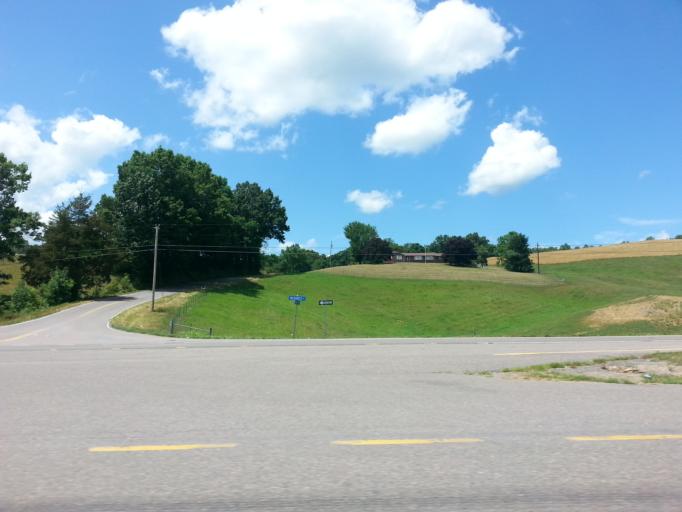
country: US
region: Virginia
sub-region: Lee County
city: Jonesville
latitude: 36.6806
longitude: -83.1554
